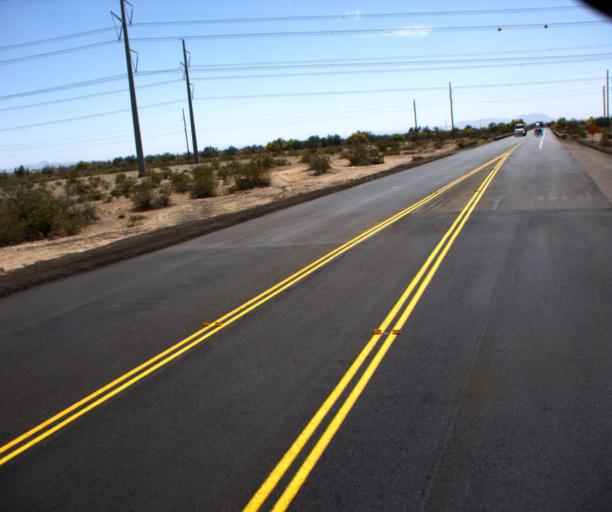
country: US
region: Arizona
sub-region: Maricopa County
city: Gila Bend
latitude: 32.9730
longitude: -112.6719
